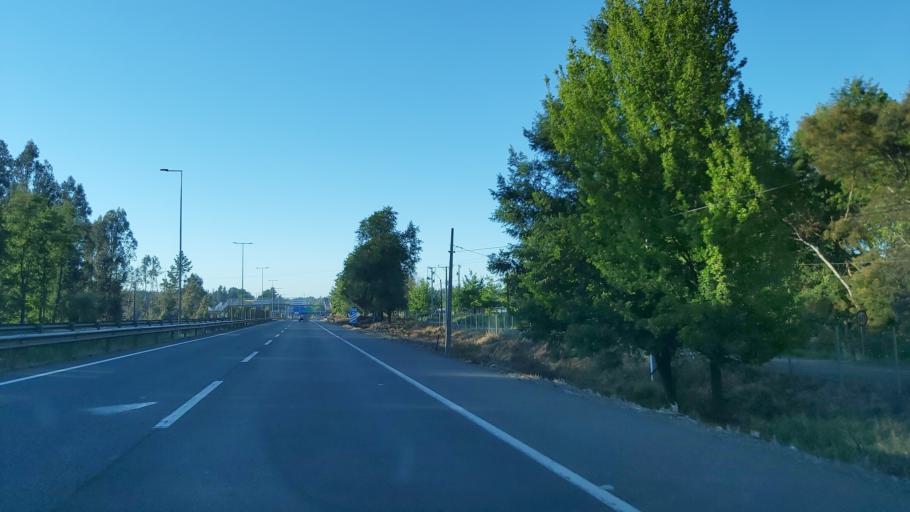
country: CL
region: Araucania
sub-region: Provincia de Malleco
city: Collipulli
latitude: -38.0702
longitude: -72.3766
